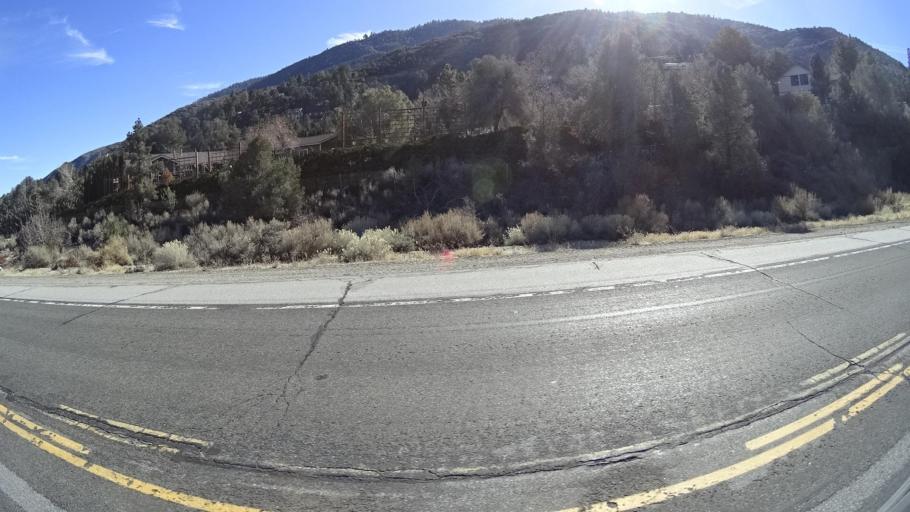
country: US
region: California
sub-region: Kern County
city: Frazier Park
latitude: 34.8212
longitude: -118.9538
